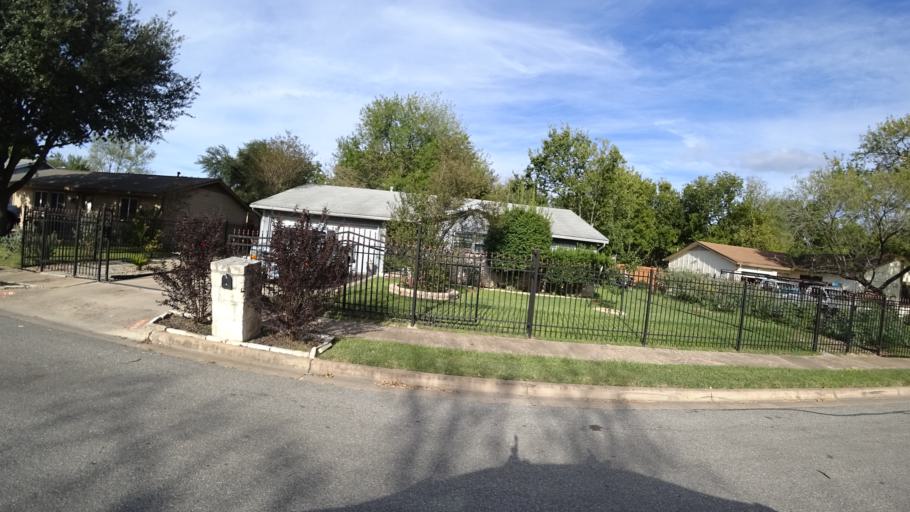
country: US
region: Texas
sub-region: Travis County
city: Onion Creek
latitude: 30.1891
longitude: -97.7549
